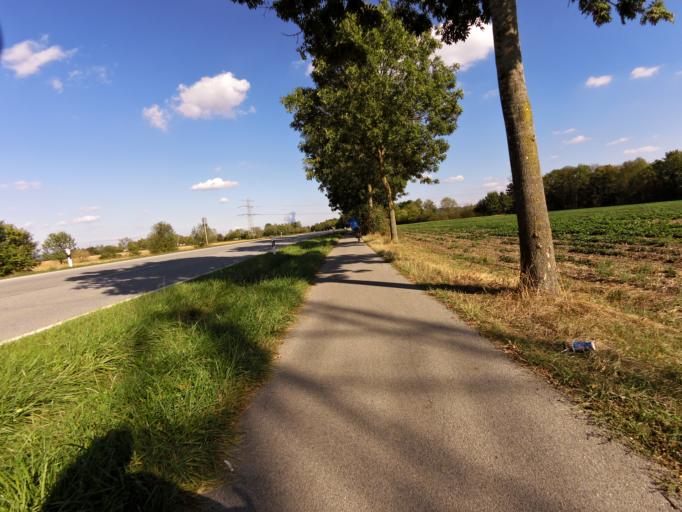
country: DE
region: Bavaria
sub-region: Lower Bavaria
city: Essenbach
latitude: 48.5888
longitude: 12.2184
